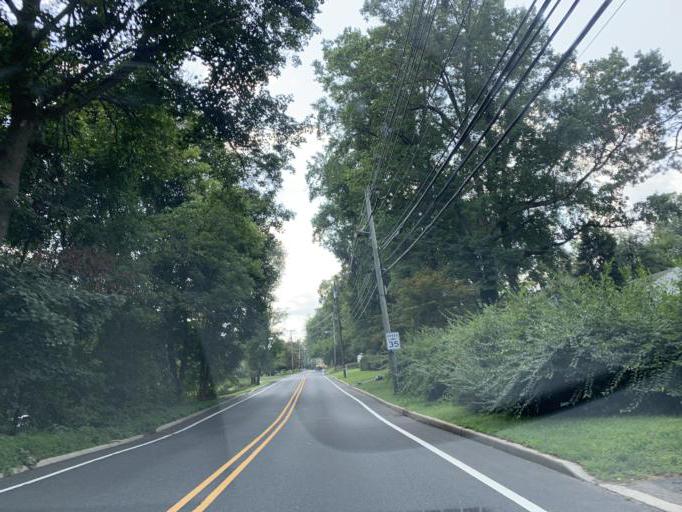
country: US
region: New Jersey
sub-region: Somerset County
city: Bernardsville
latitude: 40.7102
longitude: -74.5670
